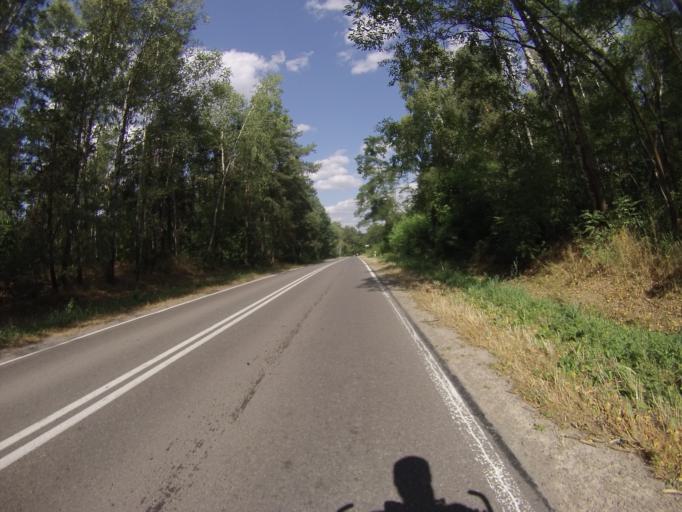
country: PL
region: Swietokrzyskie
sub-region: Powiat kielecki
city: Rakow
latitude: 50.7002
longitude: 21.0573
